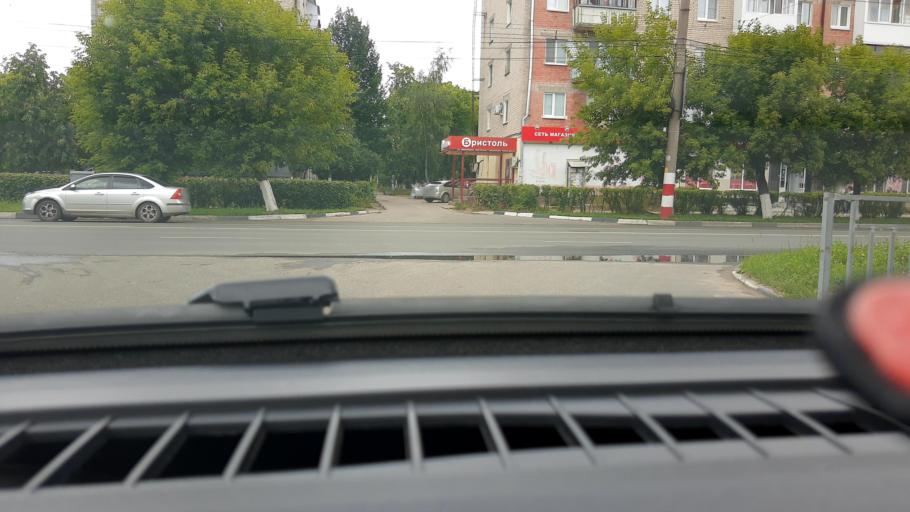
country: RU
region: Nizjnij Novgorod
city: Dzerzhinsk
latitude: 56.2339
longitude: 43.4451
